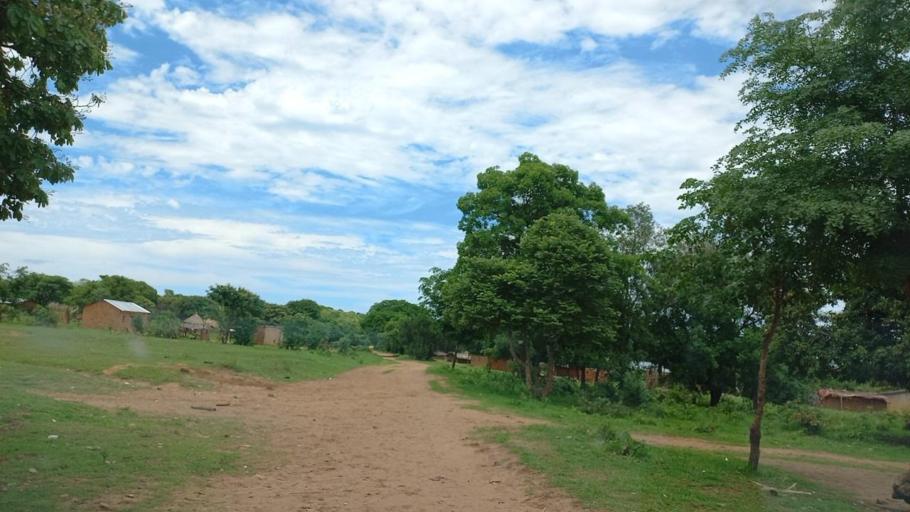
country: ZM
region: North-Western
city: Kabompo
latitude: -13.6101
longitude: 24.2458
